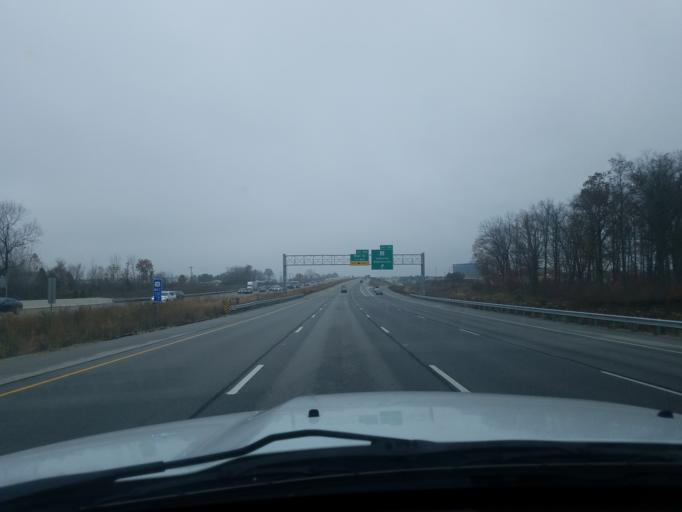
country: US
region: Indiana
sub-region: Hamilton County
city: Westfield
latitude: 40.0356
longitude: -86.1355
